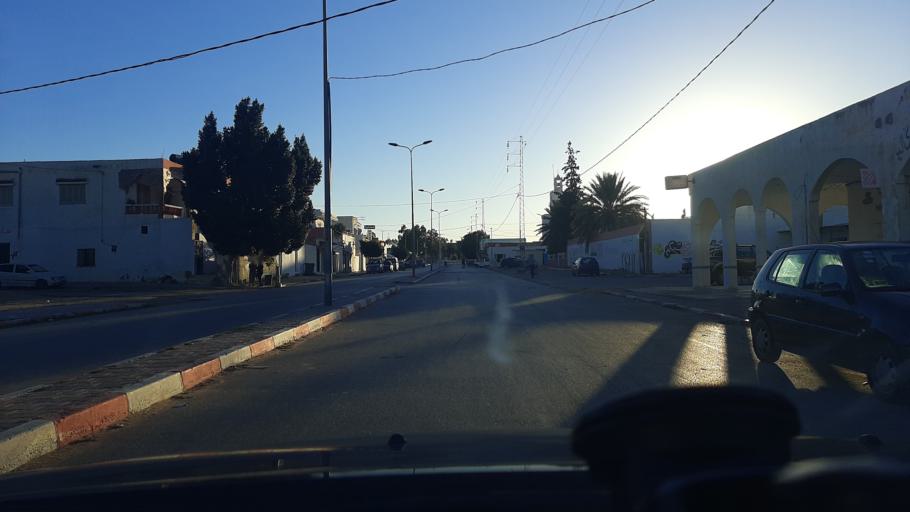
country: TN
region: Al Mahdiyah
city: Shurban
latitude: 34.9629
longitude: 10.3649
